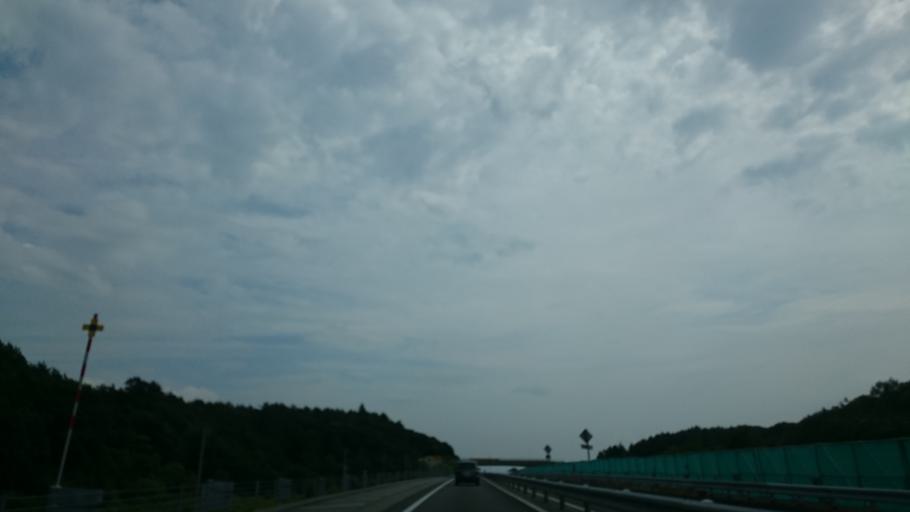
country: JP
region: Gifu
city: Gujo
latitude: 36.0096
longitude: 136.9296
